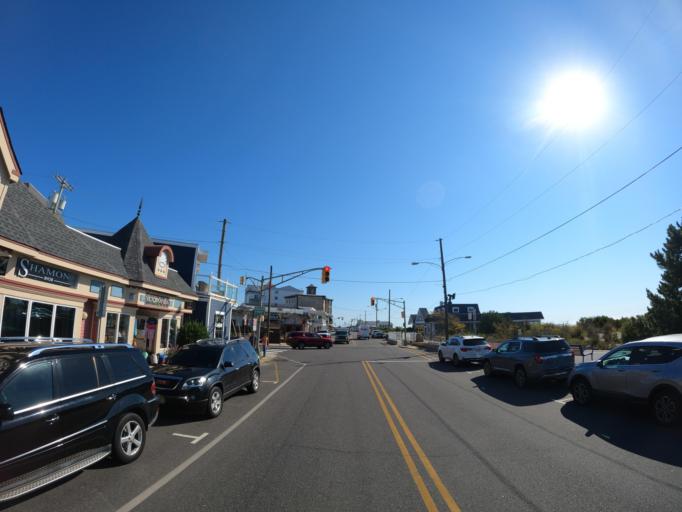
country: US
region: New Jersey
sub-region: Cape May County
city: Cape May
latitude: 38.9304
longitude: -74.9222
